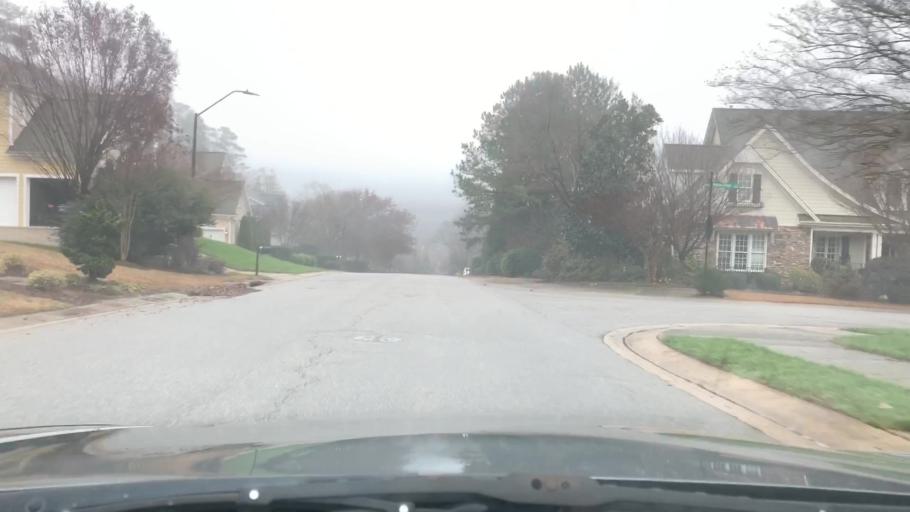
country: US
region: North Carolina
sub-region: Wake County
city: West Raleigh
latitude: 35.8471
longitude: -78.6693
